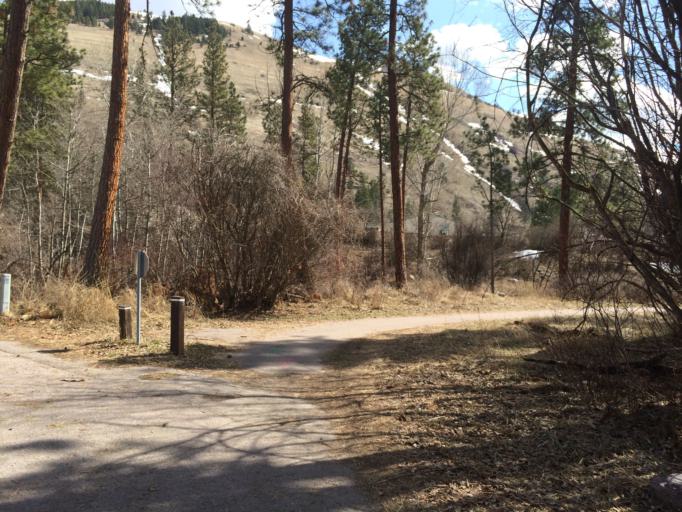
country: US
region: Montana
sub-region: Missoula County
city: Missoula
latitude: 46.8793
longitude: -113.9735
